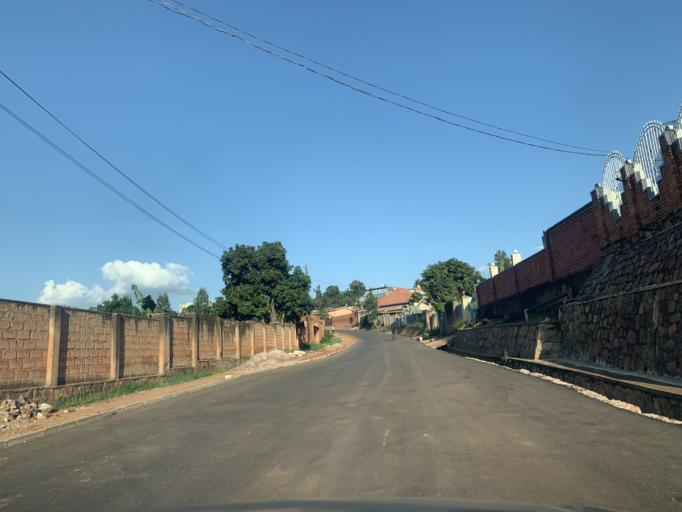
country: RW
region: Kigali
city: Kigali
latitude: -1.9678
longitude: 30.0990
